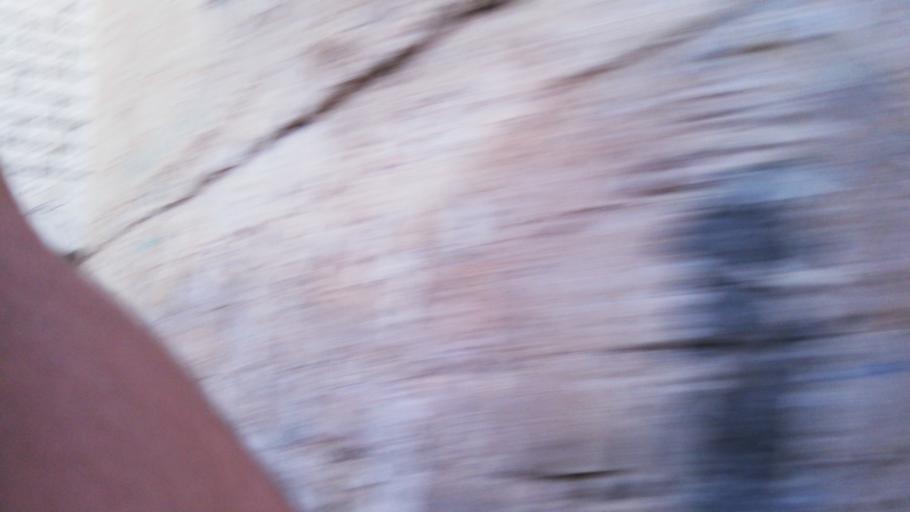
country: TR
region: Mardin
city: Kindirip
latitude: 37.4454
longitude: 41.2200
